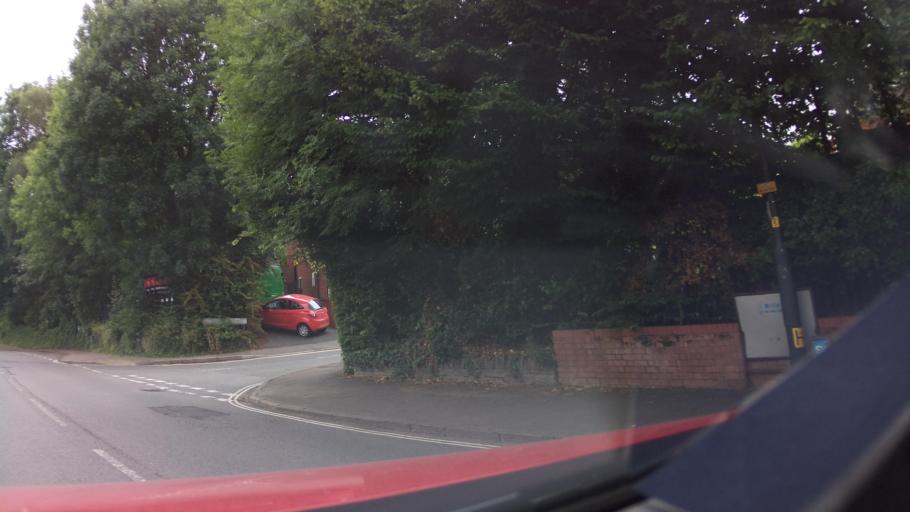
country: GB
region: England
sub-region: Worcestershire
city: Droitwich
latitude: 52.2681
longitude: -2.1457
